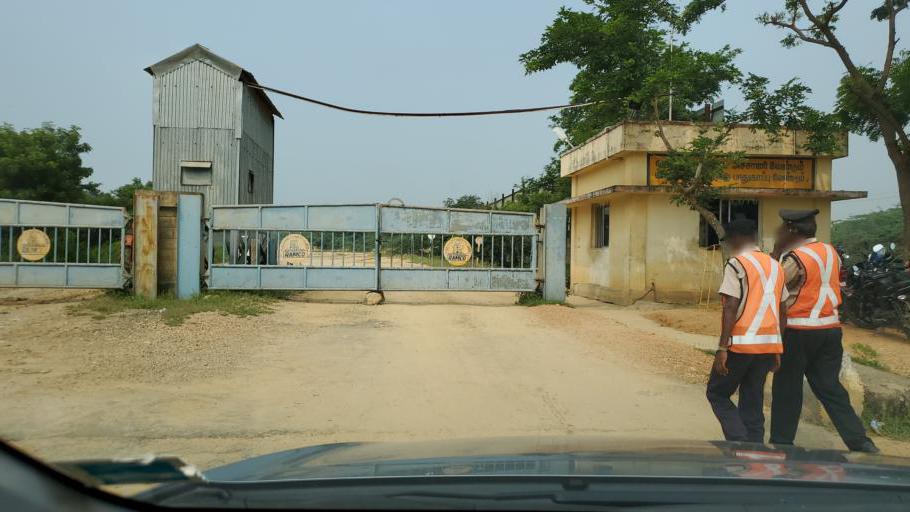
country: IN
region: Tamil Nadu
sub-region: Ariyalur
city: Ariyalur
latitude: 11.1196
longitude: 79.1459
